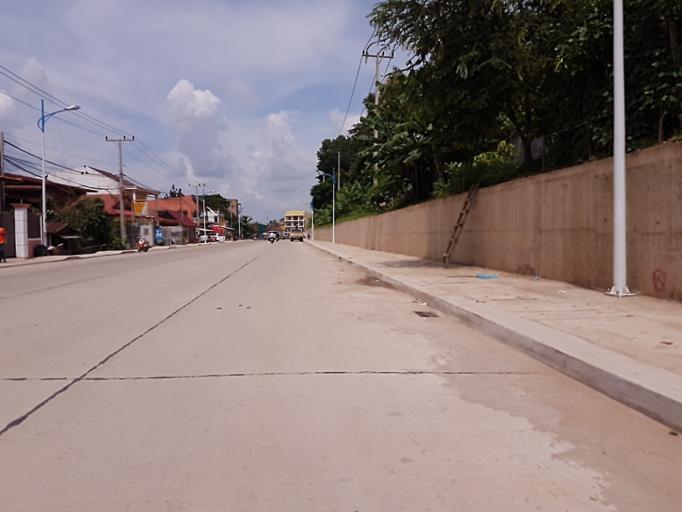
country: TH
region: Nong Khai
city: Si Chiang Mai
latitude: 17.9074
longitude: 102.6192
